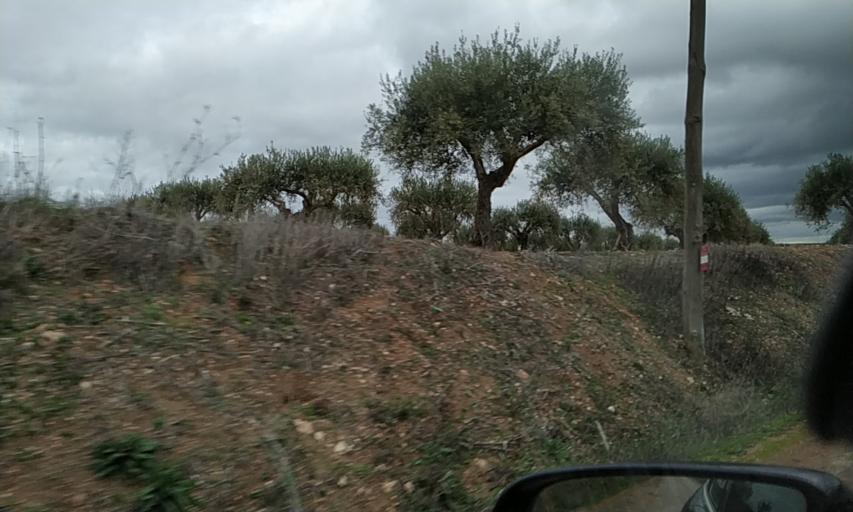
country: PT
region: Portalegre
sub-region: Campo Maior
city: Campo Maior
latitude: 38.9996
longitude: -7.0273
